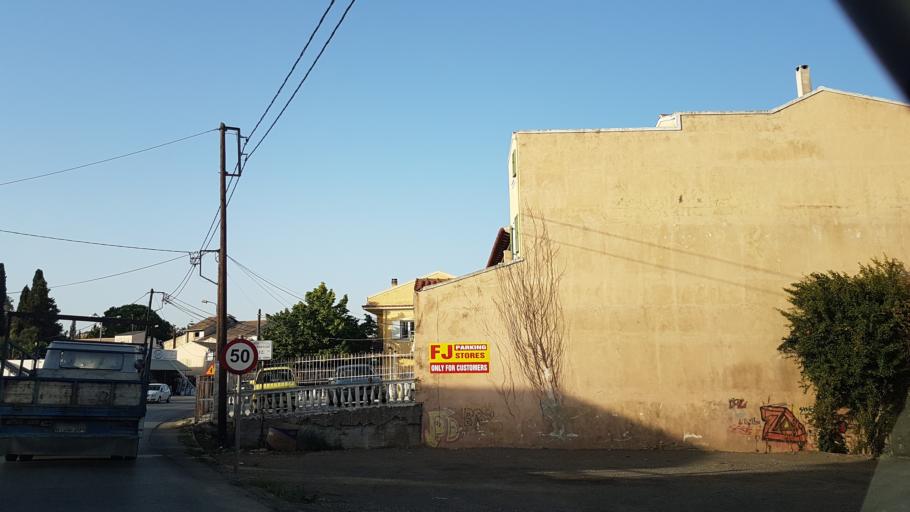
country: GR
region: Ionian Islands
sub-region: Nomos Kerkyras
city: Kanali
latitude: 39.6053
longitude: 19.8943
